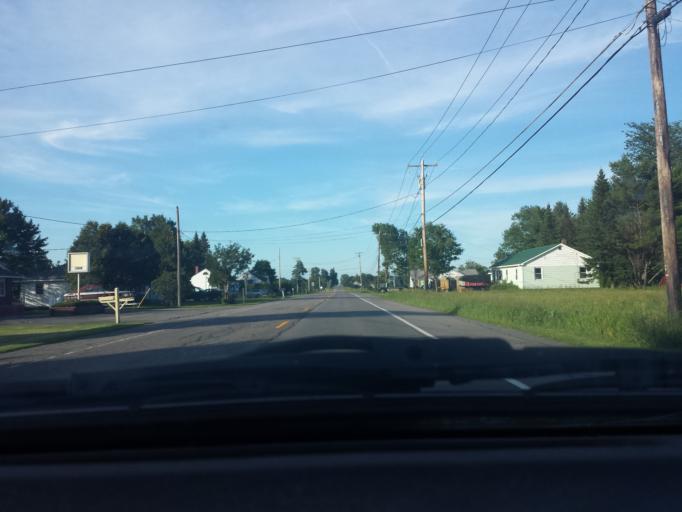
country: US
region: New York
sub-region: St. Lawrence County
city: Potsdam
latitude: 44.6829
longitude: -74.9635
